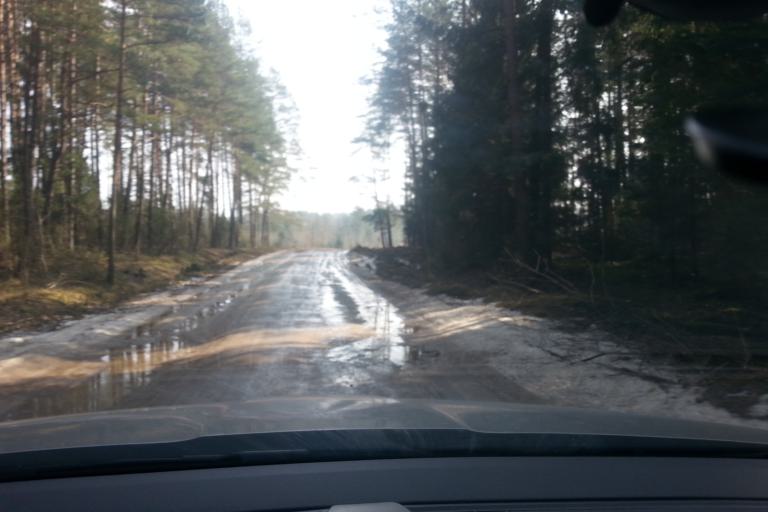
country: LT
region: Vilnius County
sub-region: Trakai
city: Rudiskes
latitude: 54.5089
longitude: 24.9413
